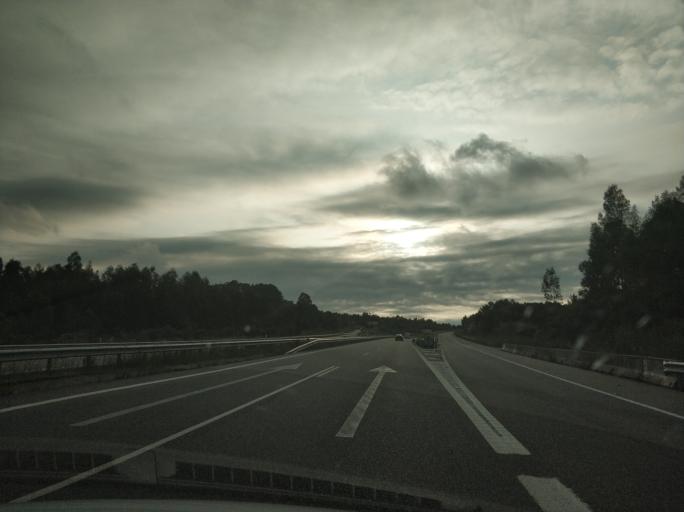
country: ES
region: Asturias
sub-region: Province of Asturias
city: Cudillero
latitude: 43.5563
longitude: -6.2012
